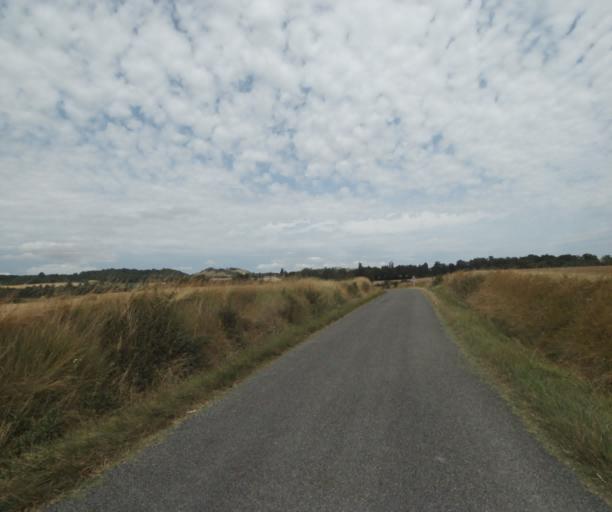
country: FR
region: Midi-Pyrenees
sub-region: Departement de la Haute-Garonne
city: Saint-Felix-Lauragais
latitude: 43.4216
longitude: 1.9004
